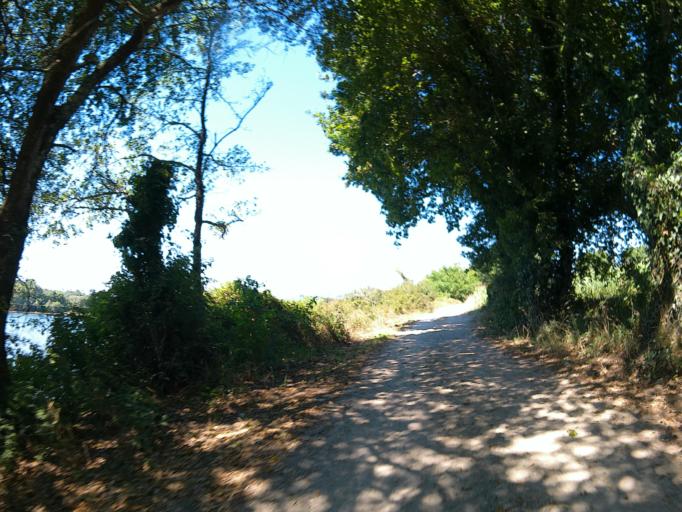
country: PT
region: Viana do Castelo
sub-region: Viana do Castelo
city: Darque
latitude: 41.7137
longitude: -8.7063
